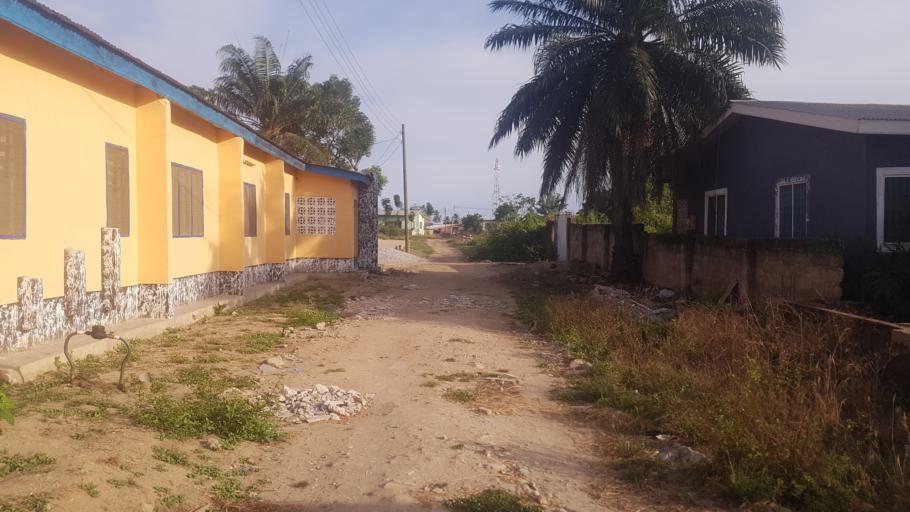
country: GH
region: Central
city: Winneba
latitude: 5.3553
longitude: -0.6308
